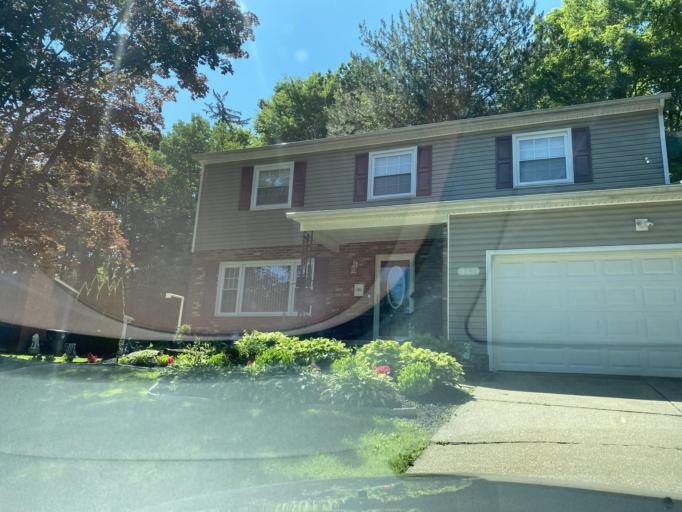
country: US
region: Ohio
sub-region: Summit County
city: Fairlawn
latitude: 41.1209
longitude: -81.5562
